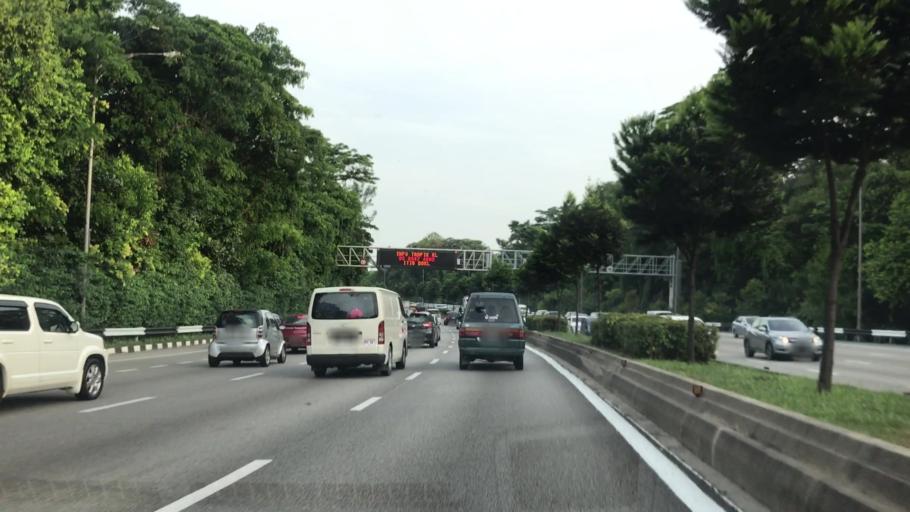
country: MY
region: Kuala Lumpur
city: Kuala Lumpur
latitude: 3.1273
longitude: 101.7023
